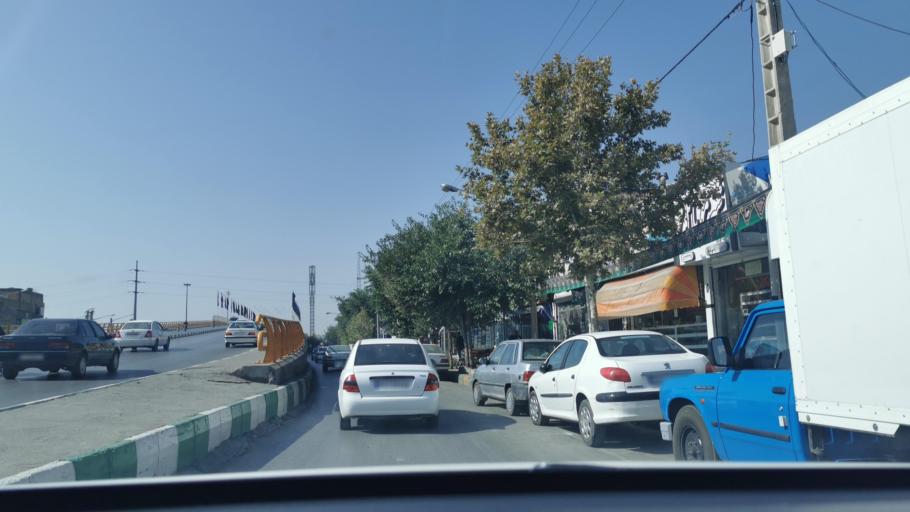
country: IR
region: Razavi Khorasan
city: Mashhad
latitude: 36.3214
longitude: 59.6403
